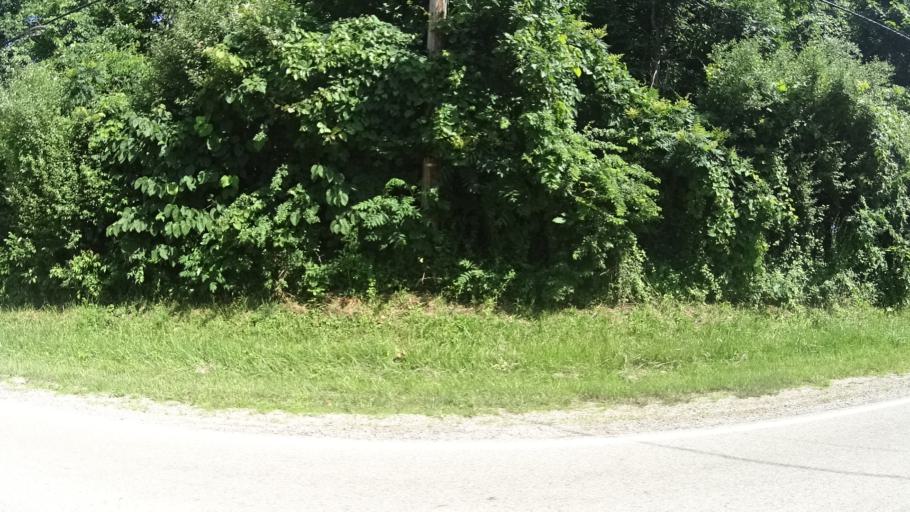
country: US
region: Ohio
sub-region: Erie County
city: Huron
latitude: 41.3319
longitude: -82.4913
